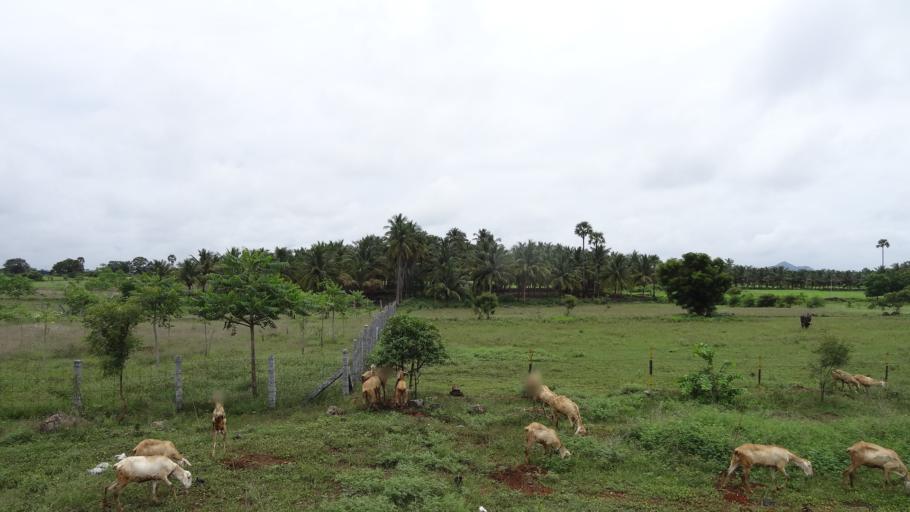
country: IN
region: Tamil Nadu
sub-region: Namakkal
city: Namakkal
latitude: 11.2916
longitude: 78.1660
